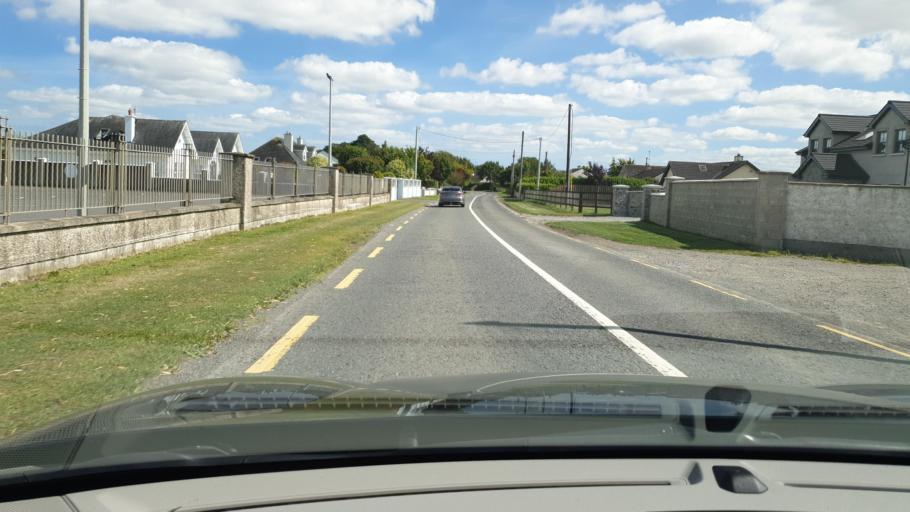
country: IE
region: Leinster
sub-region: An Mhi
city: Dunboyne
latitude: 53.4267
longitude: -6.4960
